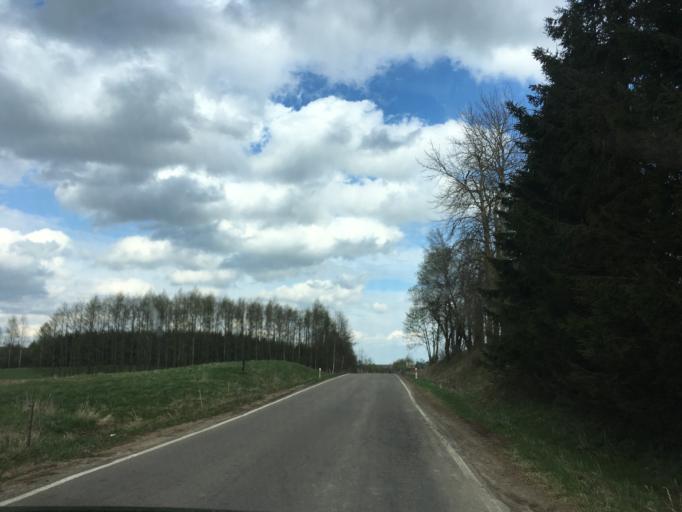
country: LT
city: Virbalis
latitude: 54.3639
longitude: 22.8472
